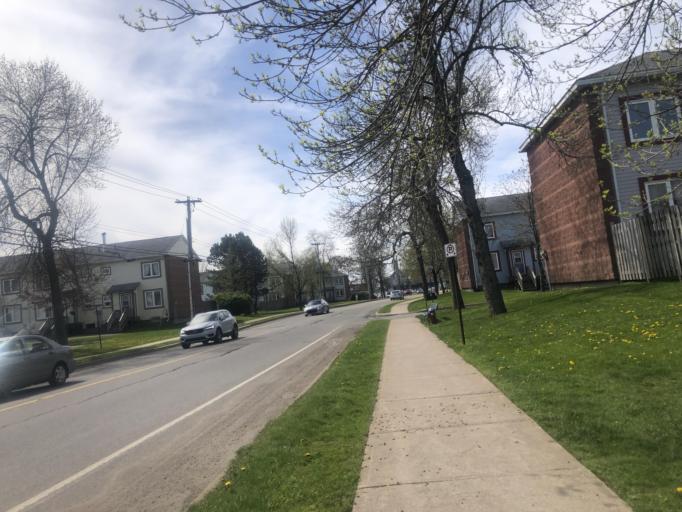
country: CA
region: New Brunswick
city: Saint John
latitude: 45.2817
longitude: -66.0780
